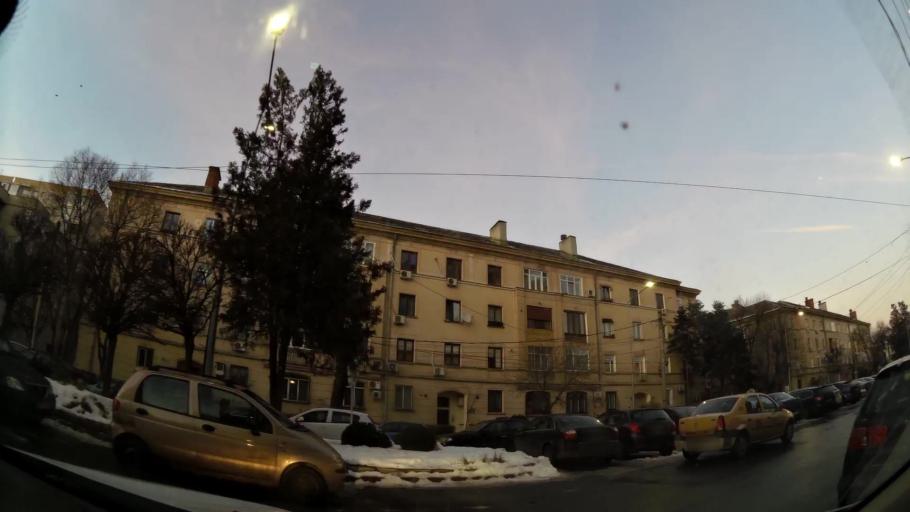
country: RO
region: Ilfov
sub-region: Comuna Fundeni-Dobroesti
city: Fundeni
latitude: 44.4355
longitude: 26.1409
